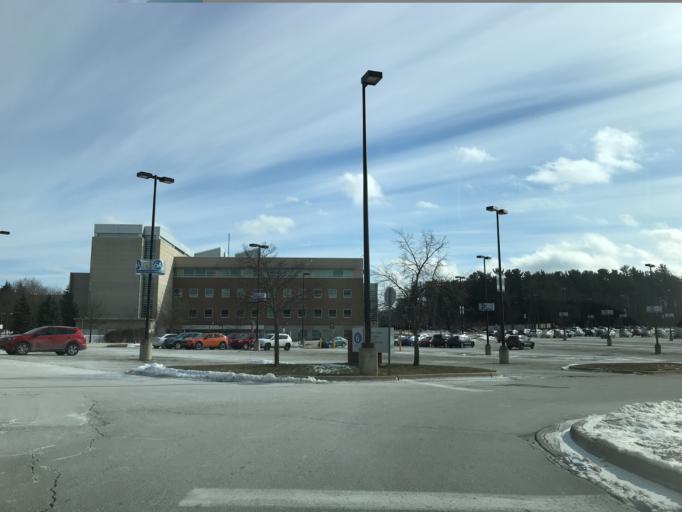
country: US
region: Michigan
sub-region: Washtenaw County
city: Ypsilanti
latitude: 42.2639
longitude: -83.6690
